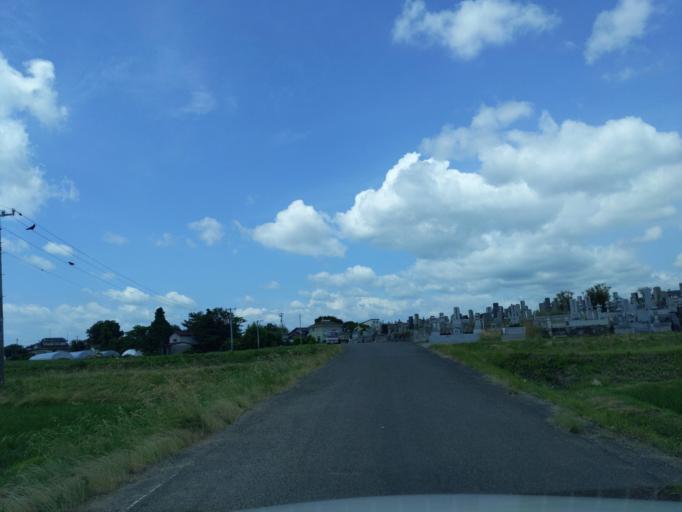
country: JP
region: Fukushima
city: Koriyama
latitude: 37.4483
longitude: 140.3562
